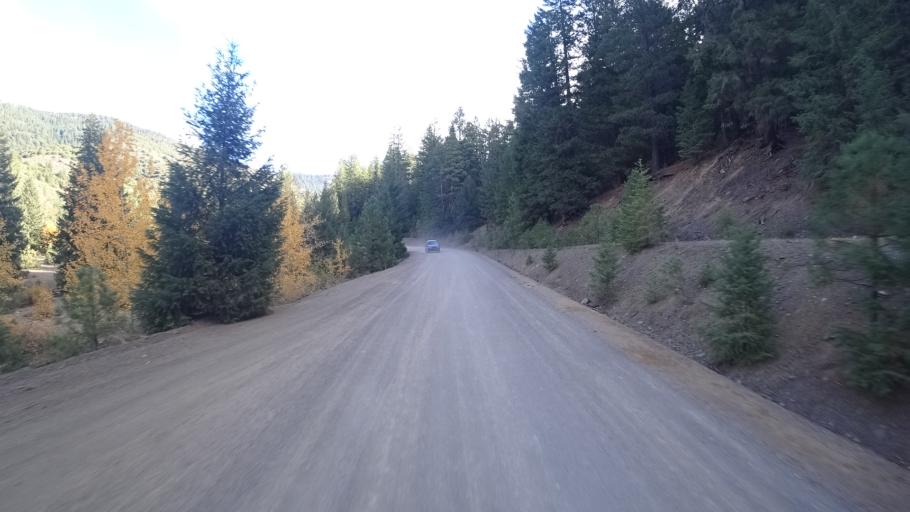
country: US
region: California
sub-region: Siskiyou County
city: Yreka
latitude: 41.7150
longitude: -122.7818
